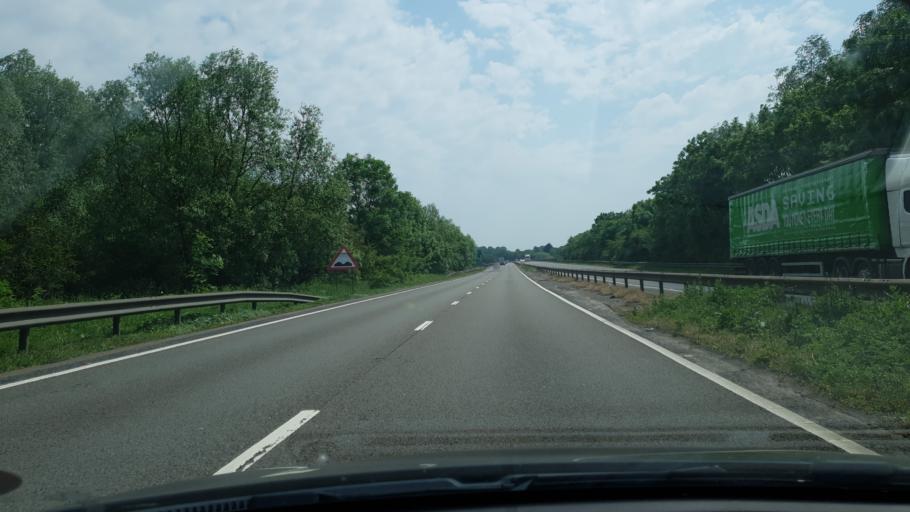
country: GB
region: England
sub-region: Northamptonshire
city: Thrapston
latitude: 52.3908
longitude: -0.5467
